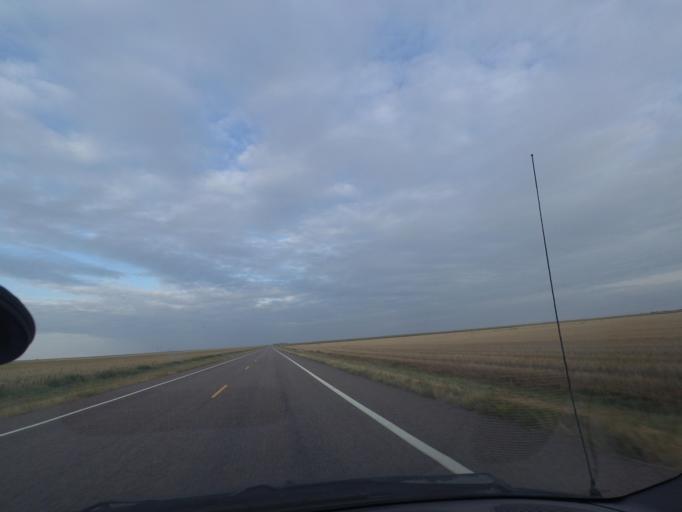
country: US
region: Colorado
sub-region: Yuma County
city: Wray
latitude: 39.7461
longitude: -102.2166
